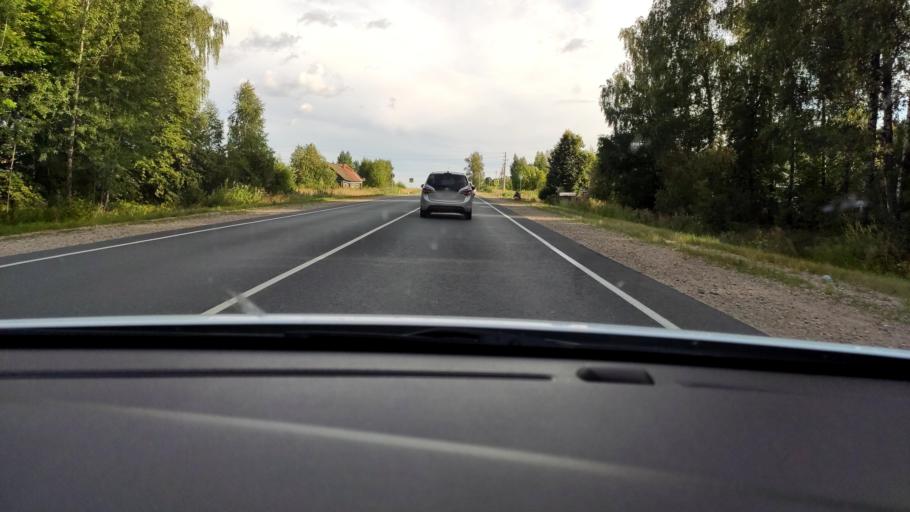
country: RU
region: Mariy-El
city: Suslonger
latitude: 56.2260
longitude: 48.2343
